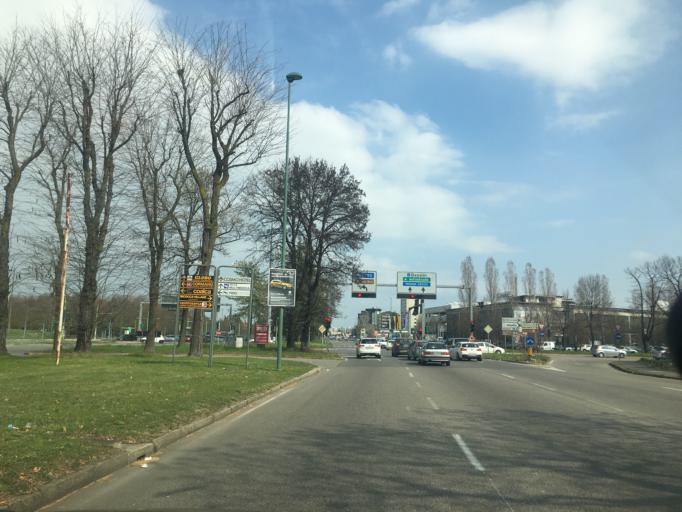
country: IT
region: Lombardy
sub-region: Citta metropolitana di Milano
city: Sesto San Giovanni
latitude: 45.5325
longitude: 9.2156
